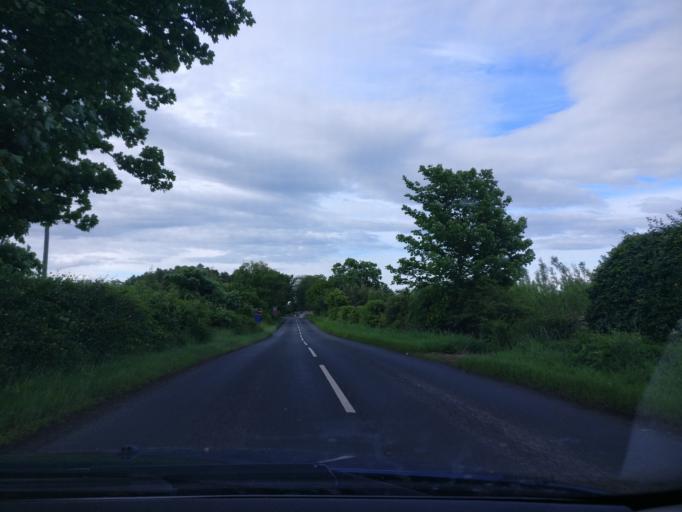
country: GB
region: Scotland
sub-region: East Lothian
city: Haddington
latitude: 55.9168
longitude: -2.7448
